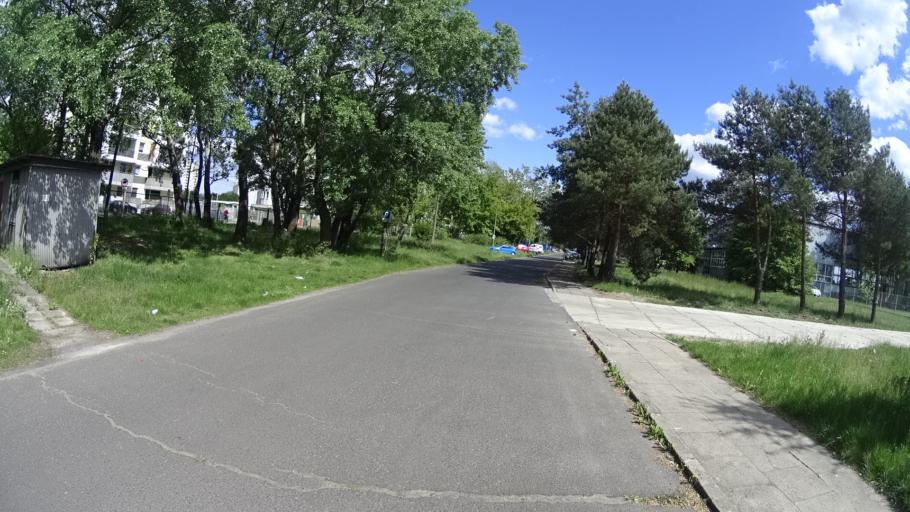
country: PL
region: Masovian Voivodeship
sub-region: Warszawa
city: Bemowo
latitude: 52.2727
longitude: 20.9117
